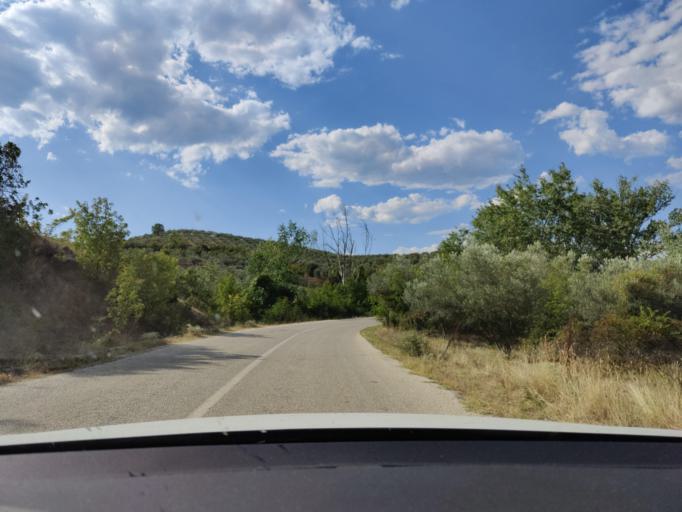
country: GR
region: Central Macedonia
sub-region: Nomos Serron
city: Chrysochorafa
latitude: 41.1439
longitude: 23.2127
